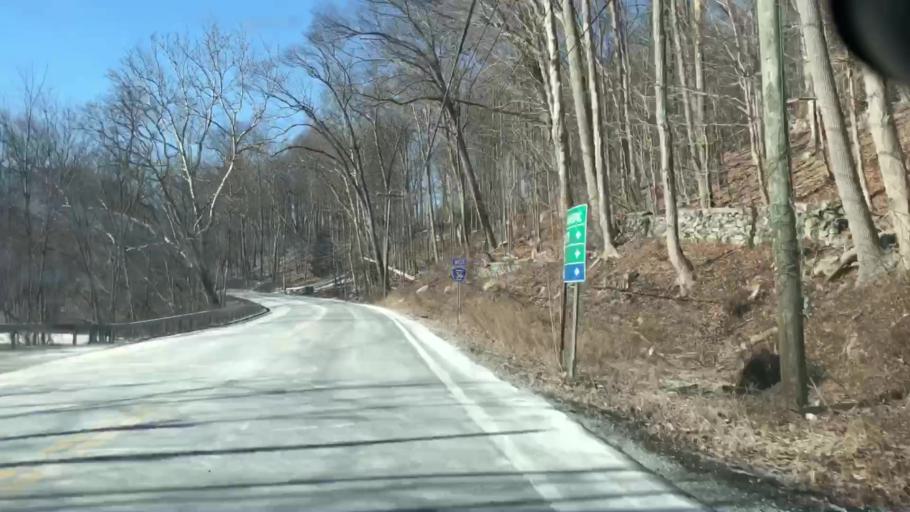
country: US
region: New York
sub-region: Putnam County
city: Carmel Hamlet
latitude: 41.3887
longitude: -73.6787
